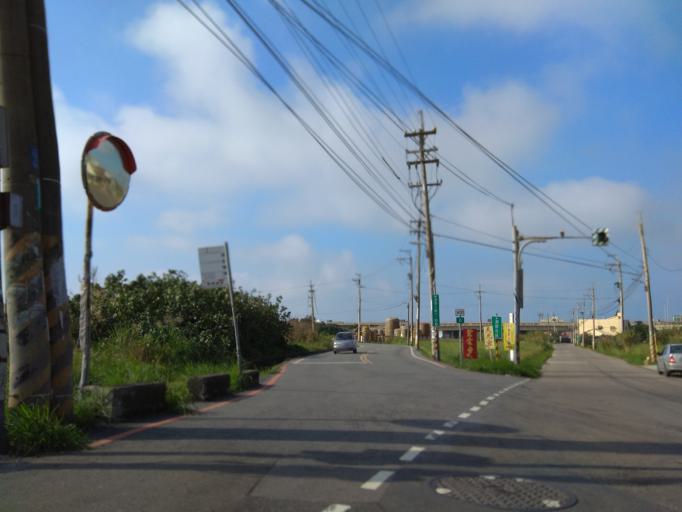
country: TW
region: Taiwan
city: Taoyuan City
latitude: 25.0785
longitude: 121.1733
